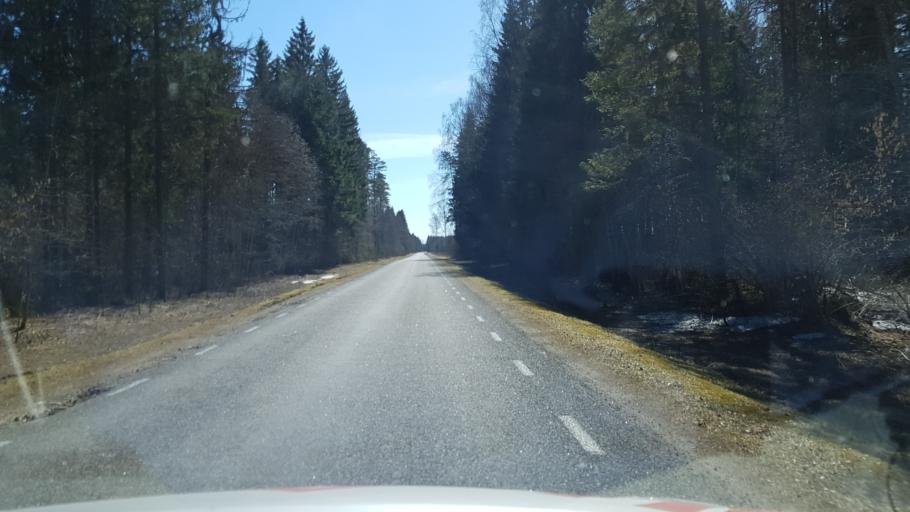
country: EE
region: Laeaene-Virumaa
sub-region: Vinni vald
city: Vinni
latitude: 59.1503
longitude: 26.5189
